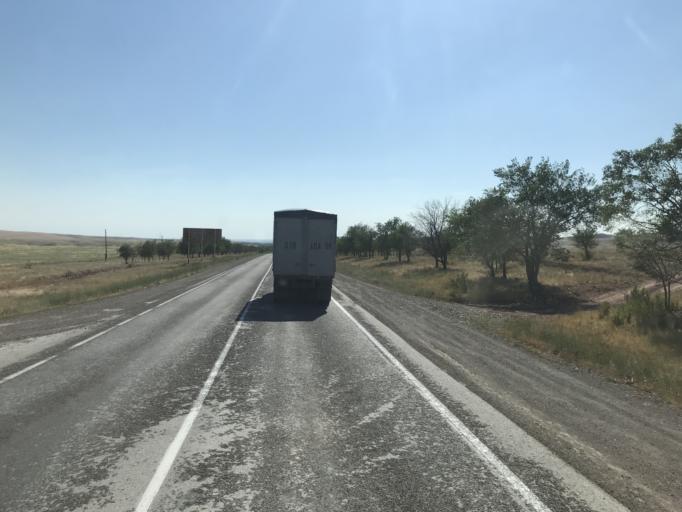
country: KZ
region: Zhambyl
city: Georgiyevka
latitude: 43.2529
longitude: 74.8084
